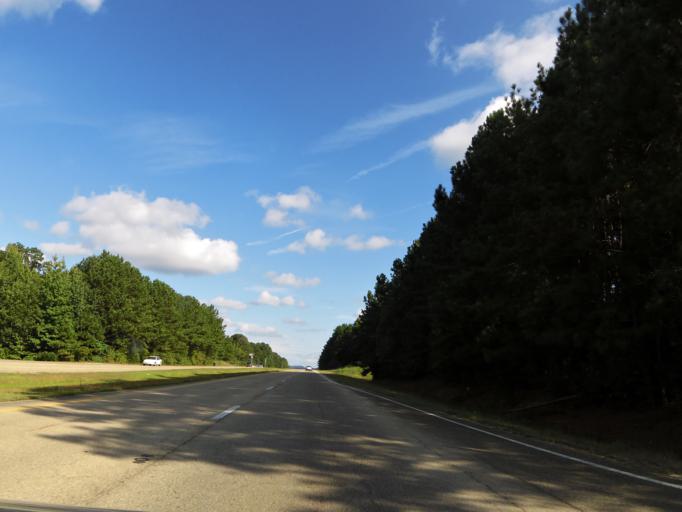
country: US
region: Mississippi
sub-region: Tishomingo County
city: Iuka
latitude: 34.8458
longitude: -88.3322
